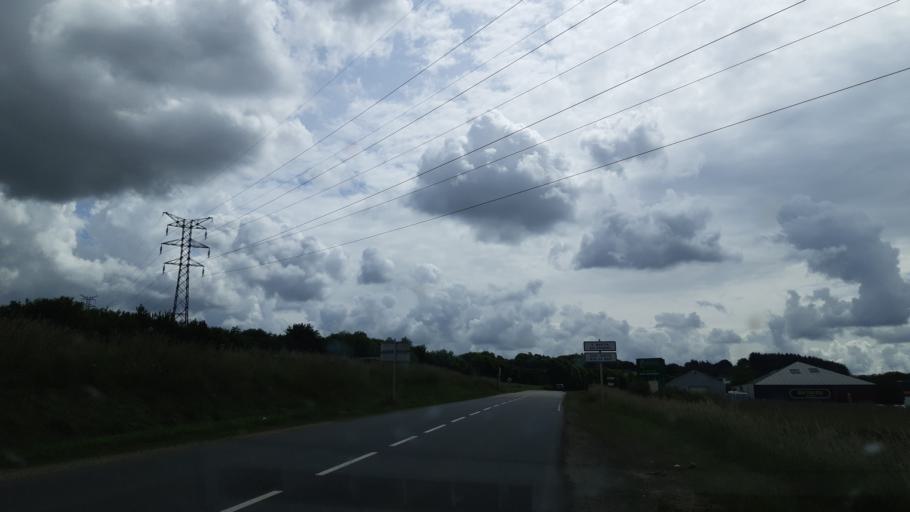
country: FR
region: Brittany
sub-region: Departement du Finistere
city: Taule
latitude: 48.5820
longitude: -3.8701
